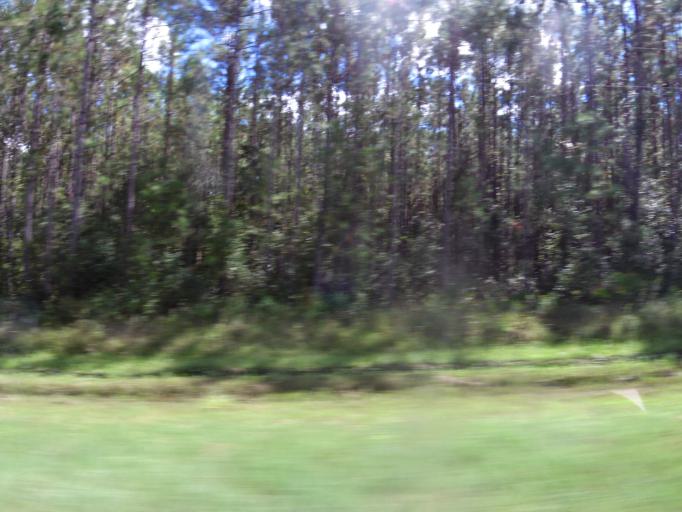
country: US
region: Florida
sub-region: Hamilton County
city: Jasper
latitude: 30.6304
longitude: -82.5991
